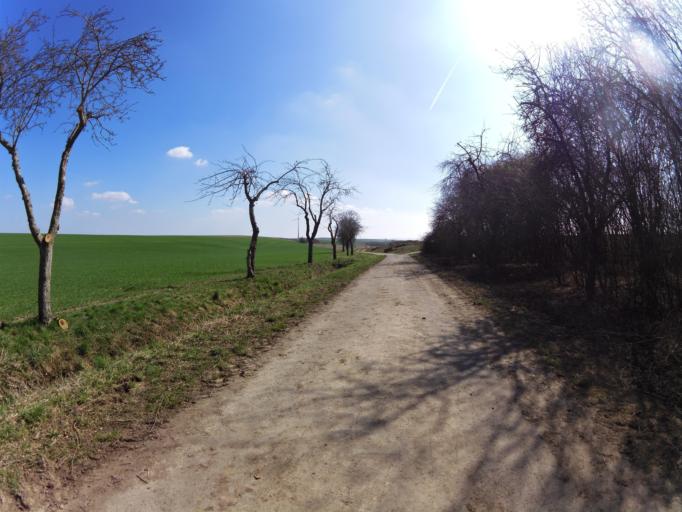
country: DE
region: Bavaria
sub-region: Regierungsbezirk Unterfranken
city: Prosselsheim
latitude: 49.8394
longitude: 10.1321
